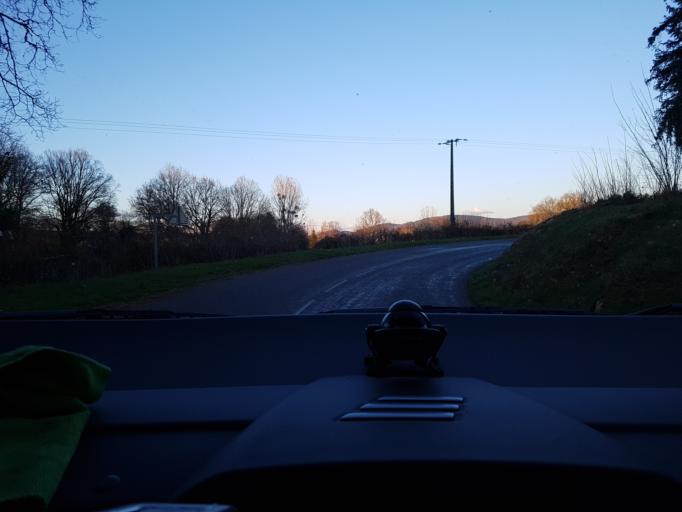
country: FR
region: Bourgogne
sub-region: Departement de Saone-et-Loire
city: Etang-sur-Arroux
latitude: 46.8973
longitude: 4.1422
